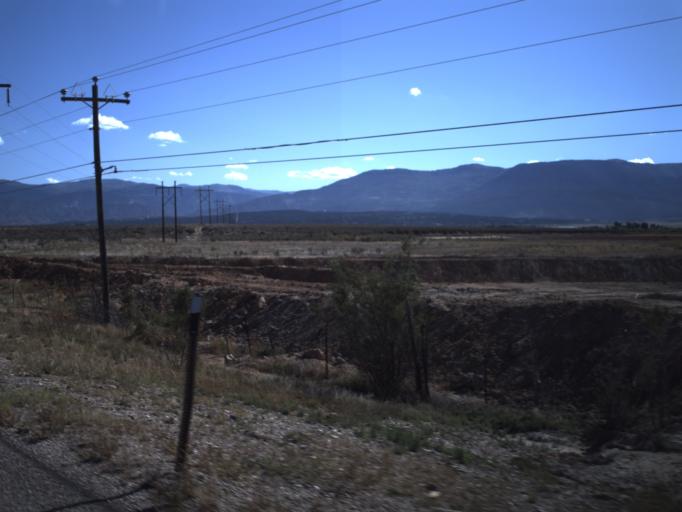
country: US
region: Utah
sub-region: Iron County
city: Cedar City
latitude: 37.6626
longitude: -113.2081
